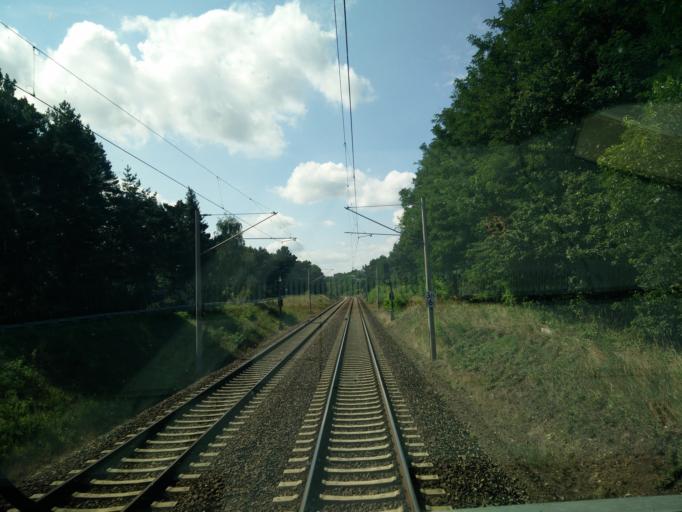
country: DE
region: Brandenburg
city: Bestensee
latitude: 52.2195
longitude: 13.6204
